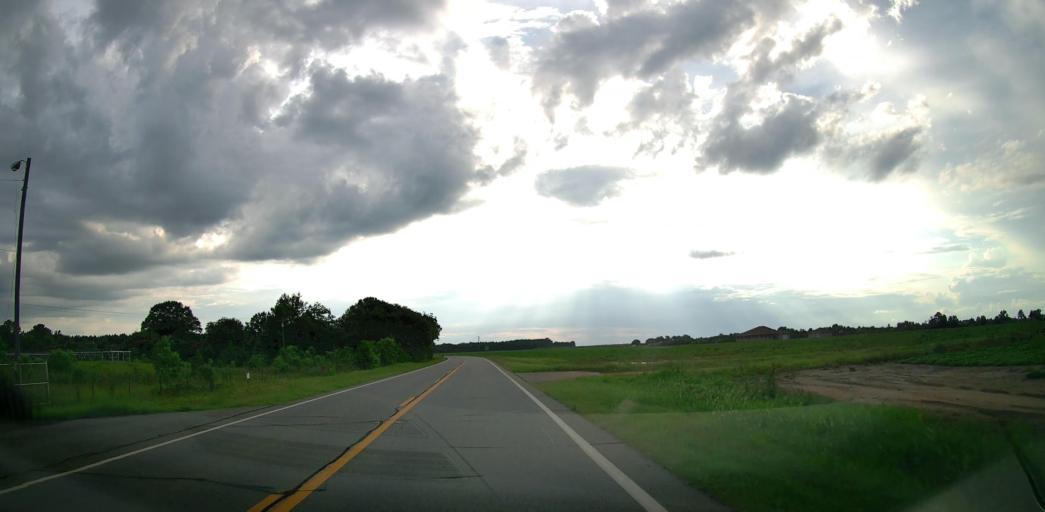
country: US
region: Georgia
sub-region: Pulaski County
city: Hawkinsville
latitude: 32.2961
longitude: -83.5334
